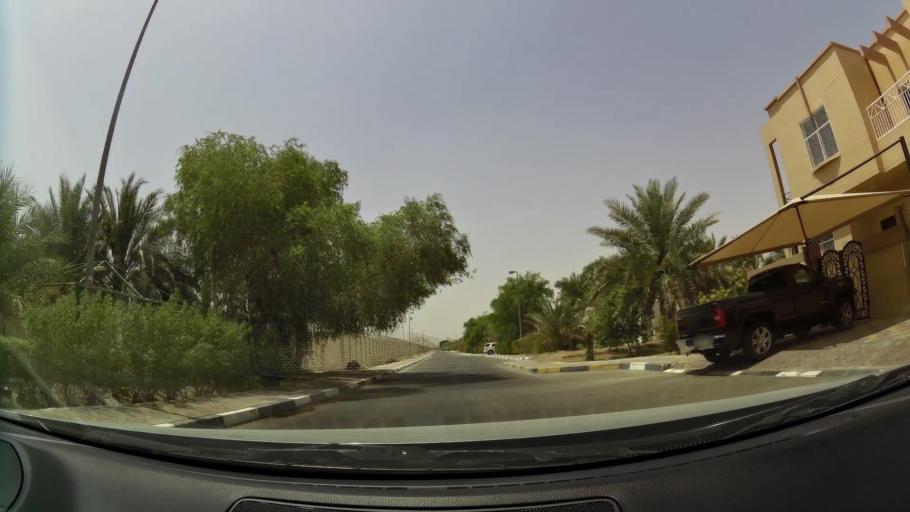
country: AE
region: Abu Dhabi
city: Al Ain
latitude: 24.1953
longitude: 55.7423
